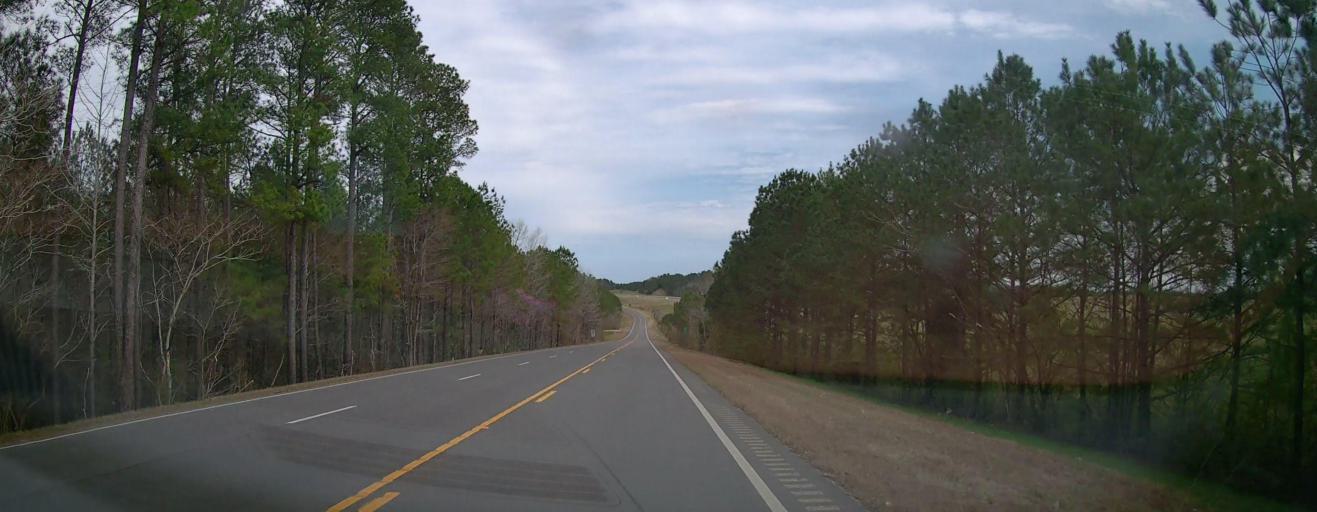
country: US
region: Alabama
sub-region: Walker County
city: Jasper
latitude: 33.8609
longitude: -87.3831
